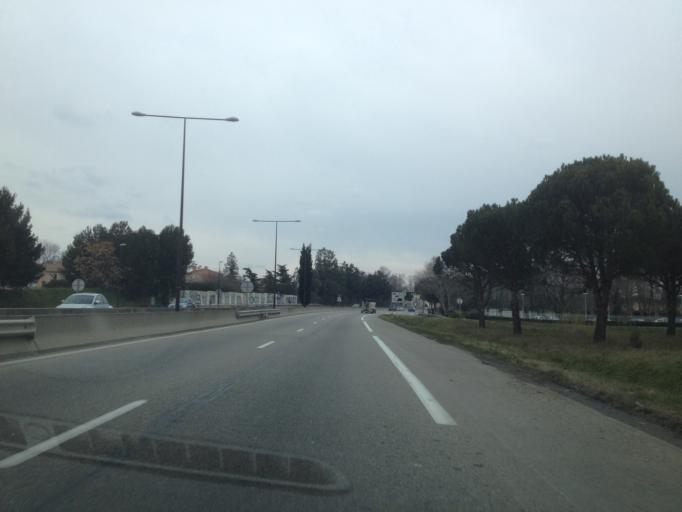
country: FR
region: Provence-Alpes-Cote d'Azur
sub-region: Departement du Vaucluse
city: Avignon
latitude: 43.9418
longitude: 4.8328
